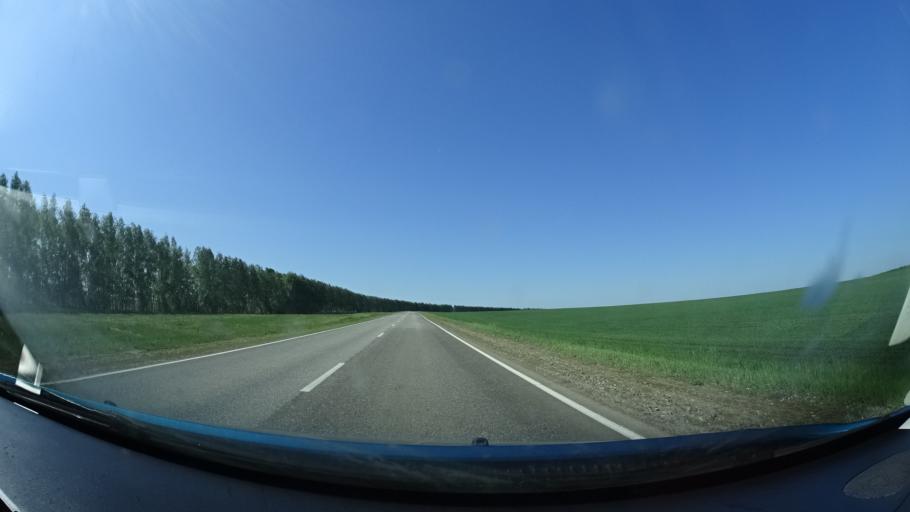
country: RU
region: Bashkortostan
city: Starobaltachevo
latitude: 55.9137
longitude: 55.7744
